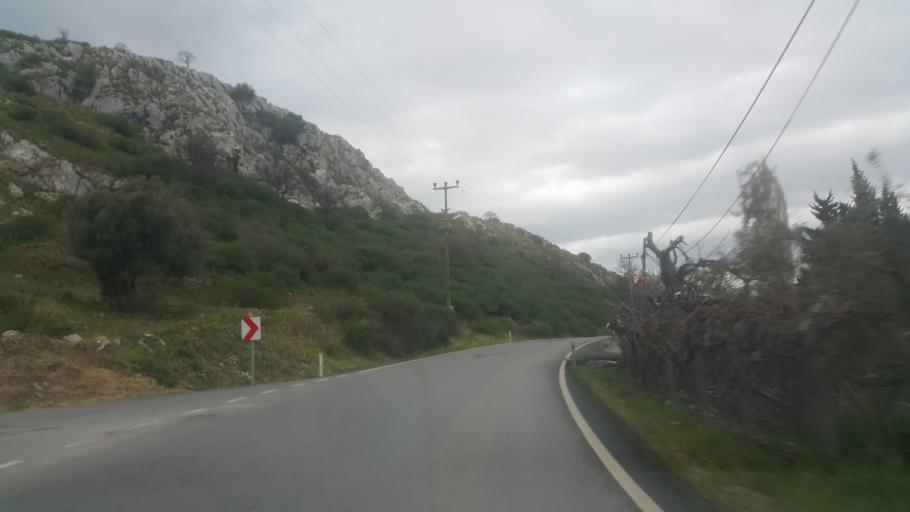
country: TR
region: Izmir
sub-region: Seferihisar
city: Seferhisar
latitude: 38.1903
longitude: 26.8059
